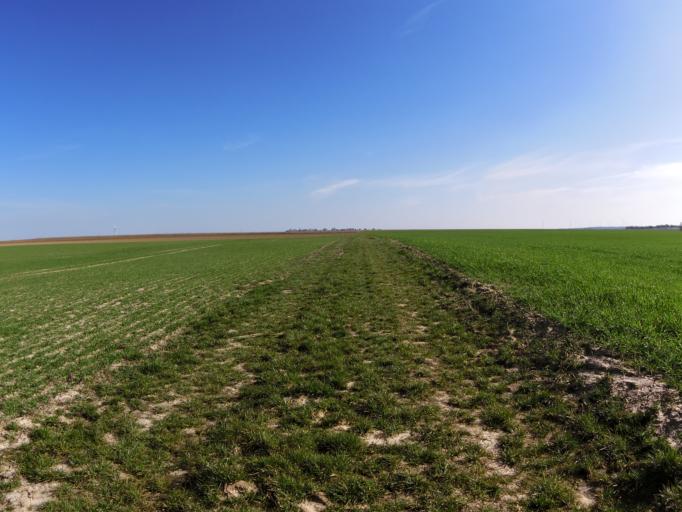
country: DE
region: Bavaria
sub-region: Regierungsbezirk Unterfranken
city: Prosselsheim
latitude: 49.8518
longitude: 10.1089
